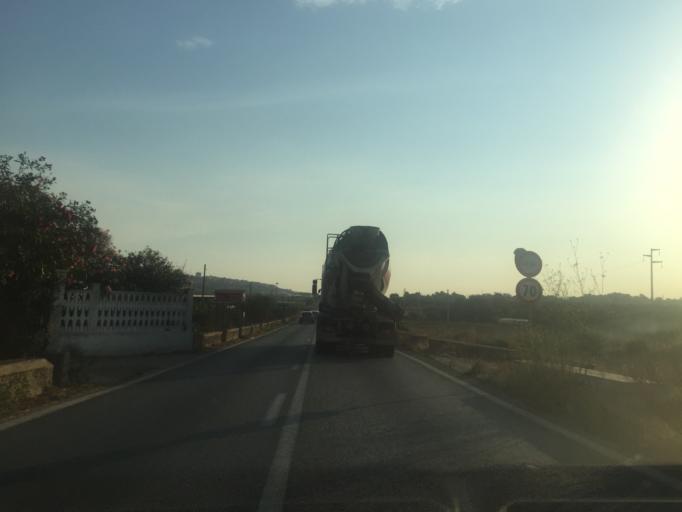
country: IT
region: Sicily
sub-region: Ragusa
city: Ispica
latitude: 36.7599
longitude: 14.8949
